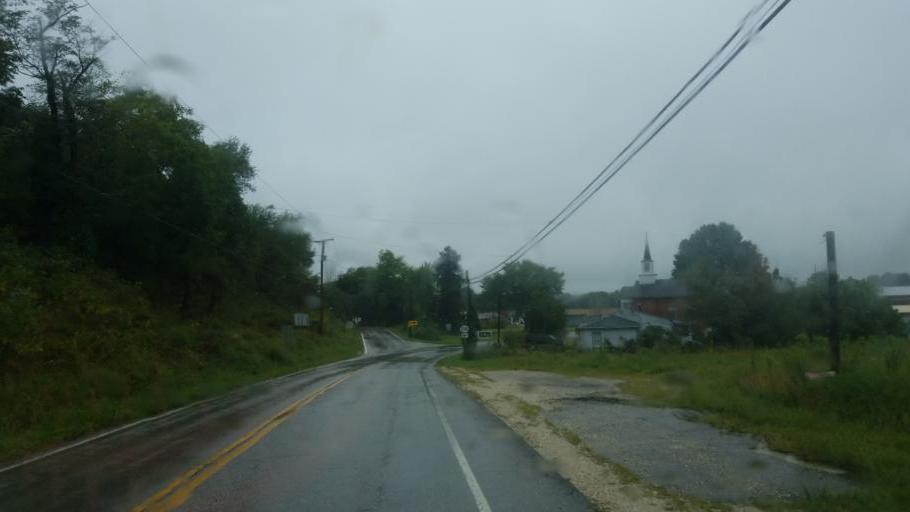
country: US
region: Kentucky
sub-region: Greenup County
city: South Shore
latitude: 38.7171
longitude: -82.9603
